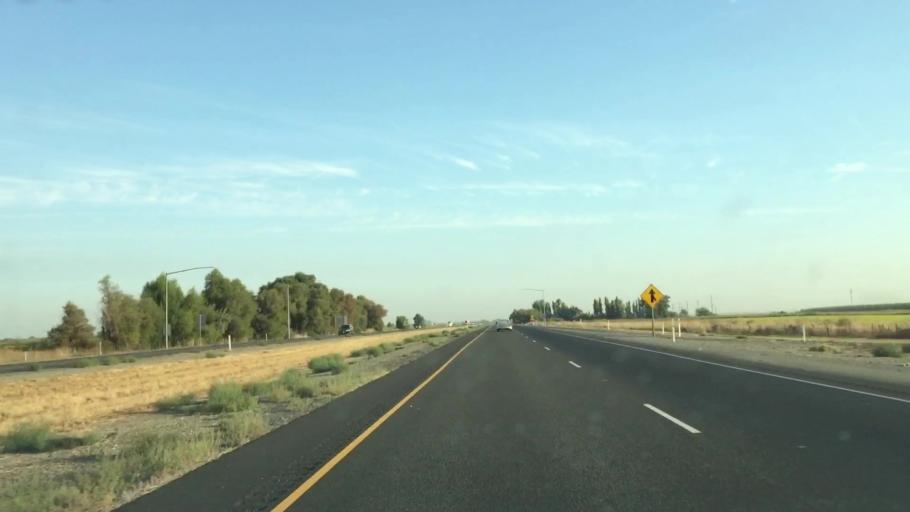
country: US
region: California
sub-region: Colusa County
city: Maxwell
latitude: 39.2788
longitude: -122.1823
